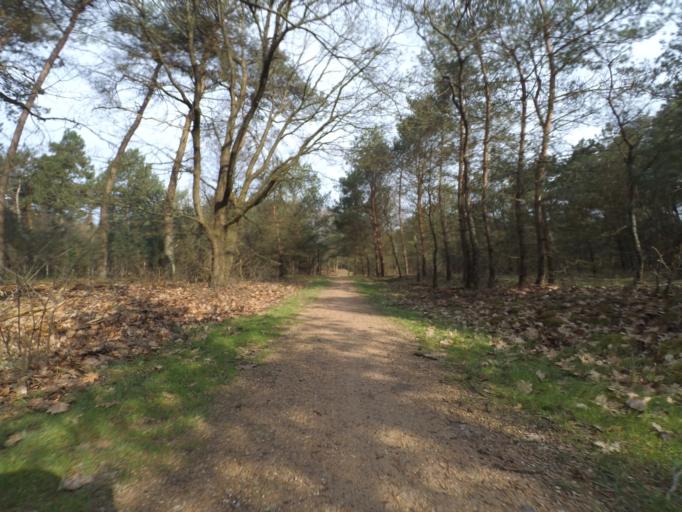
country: NL
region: Gelderland
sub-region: Gemeente Ede
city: Harskamp
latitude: 52.1605
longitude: 5.7301
